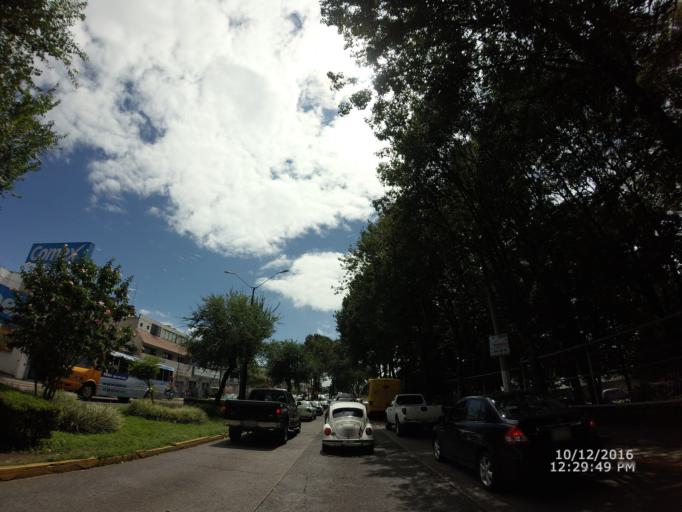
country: MX
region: Veracruz
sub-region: Xalapa
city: Xalapa de Enriquez
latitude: 19.5417
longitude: -96.9266
